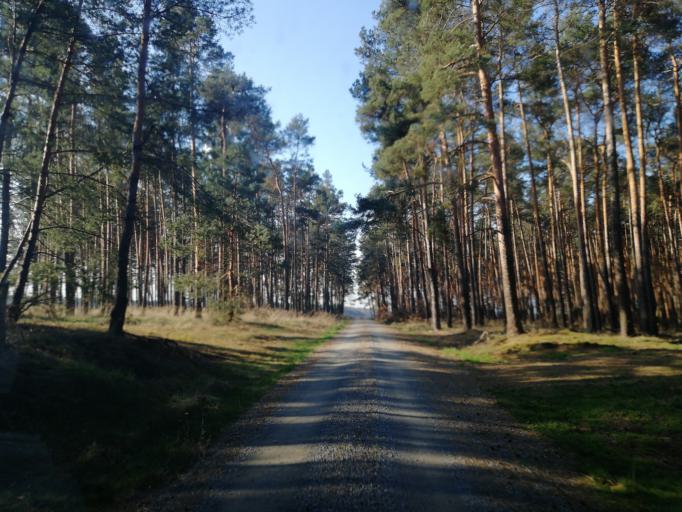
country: DE
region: Brandenburg
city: Drahnsdorf
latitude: 51.8897
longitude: 13.5256
